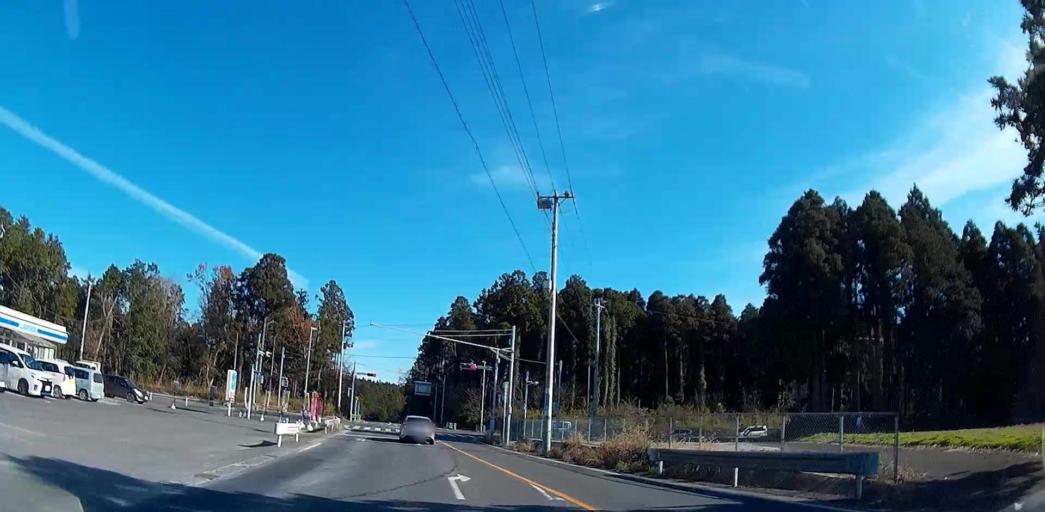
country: JP
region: Chiba
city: Yokaichiba
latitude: 35.7590
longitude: 140.4557
